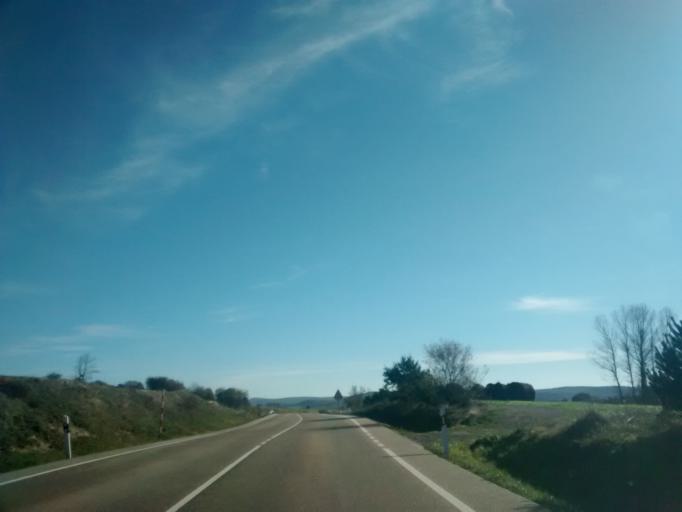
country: ES
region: Cantabria
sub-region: Provincia de Cantabria
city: San Pedro del Romeral
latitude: 42.9812
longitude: -3.8102
